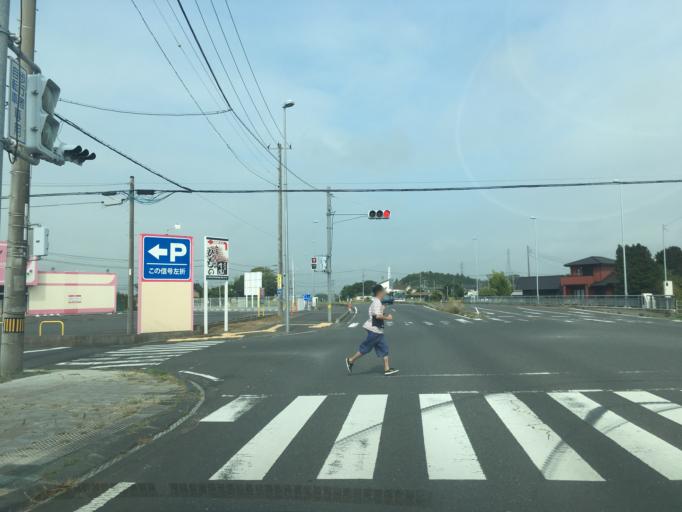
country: JP
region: Ibaraki
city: Oarai
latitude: 36.3499
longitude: 140.5782
